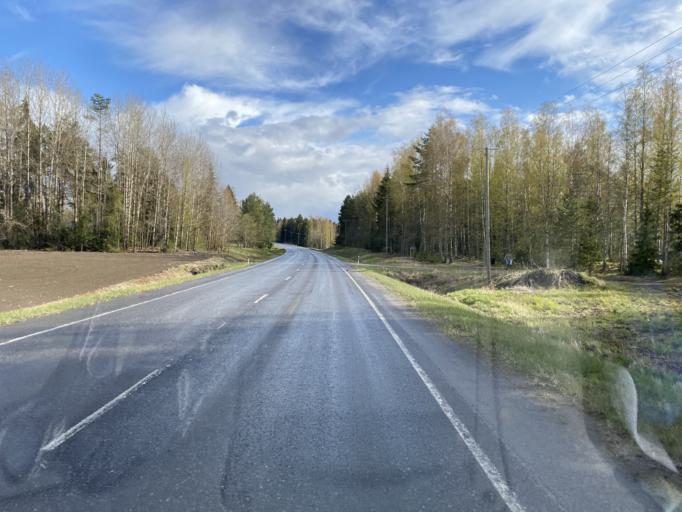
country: FI
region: Pirkanmaa
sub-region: Etelae-Pirkanmaa
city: Viiala
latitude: 61.2421
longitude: 23.7383
